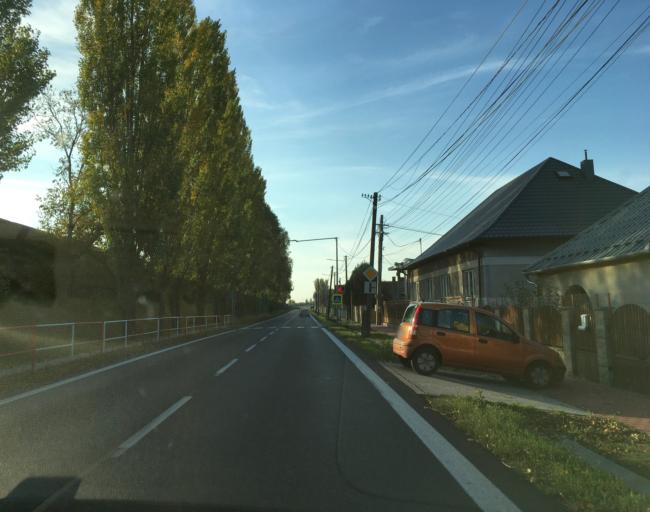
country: SK
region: Nitriansky
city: Sellye
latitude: 48.1518
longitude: 17.9367
